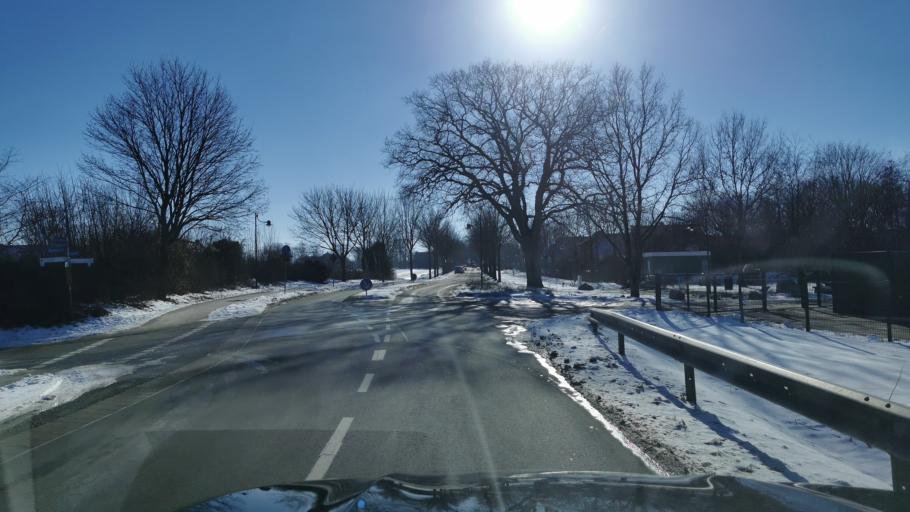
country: DE
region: Schleswig-Holstein
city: Langballig
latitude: 54.8030
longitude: 9.6380
